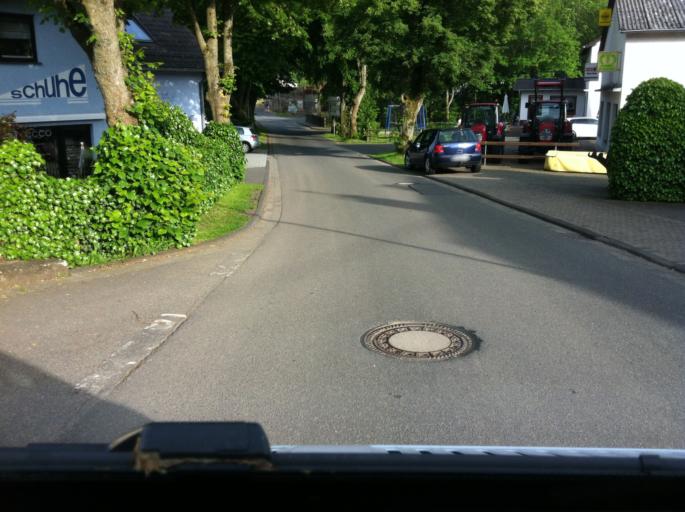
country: DE
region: Rheinland-Pfalz
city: Kerschenbach
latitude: 50.3607
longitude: 6.4762
